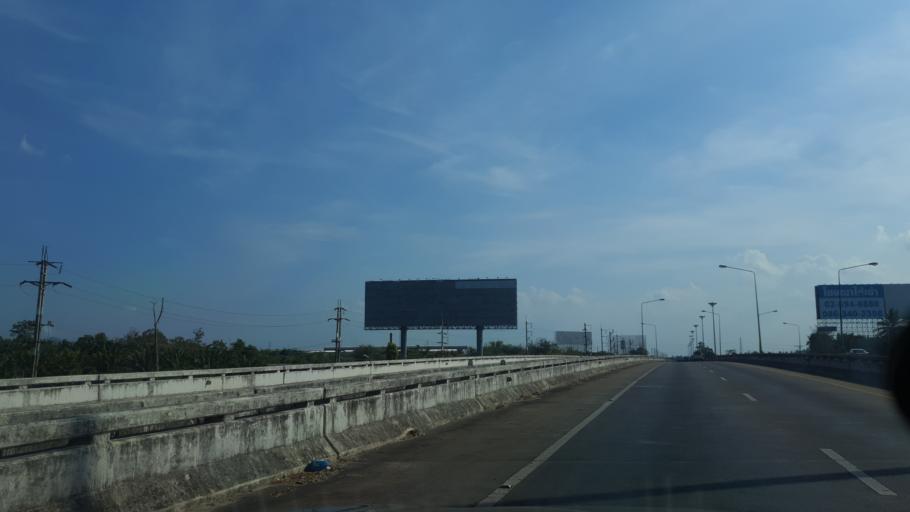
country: TH
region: Surat Thani
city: Phunphin
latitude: 9.1182
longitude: 99.1608
